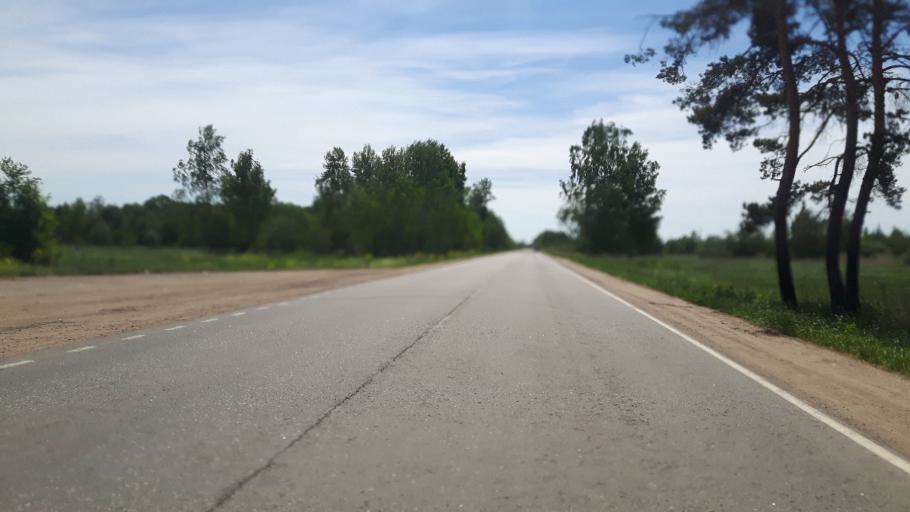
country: RU
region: Leningrad
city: Ust'-Luga
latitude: 59.5770
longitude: 28.1751
